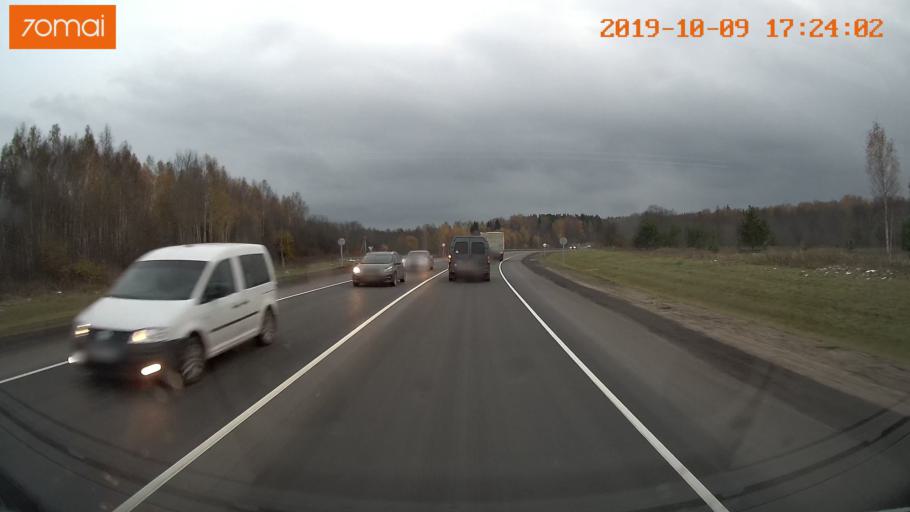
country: RU
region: Ivanovo
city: Furmanov
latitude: 57.1888
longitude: 41.1120
